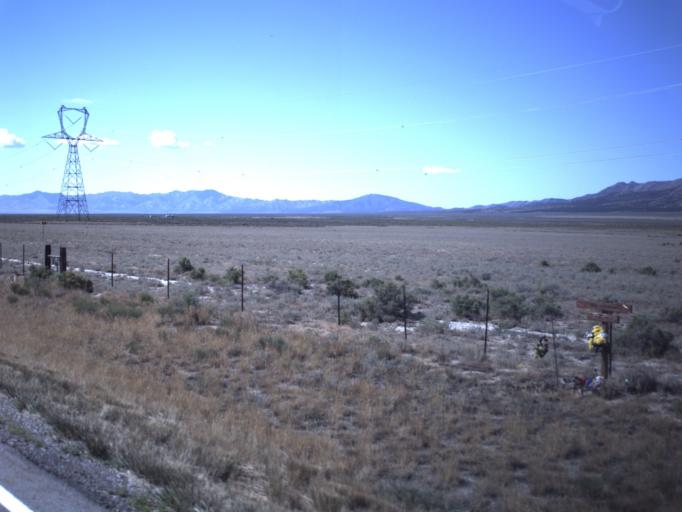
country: US
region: Utah
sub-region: Tooele County
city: Tooele
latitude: 40.2787
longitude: -112.3984
